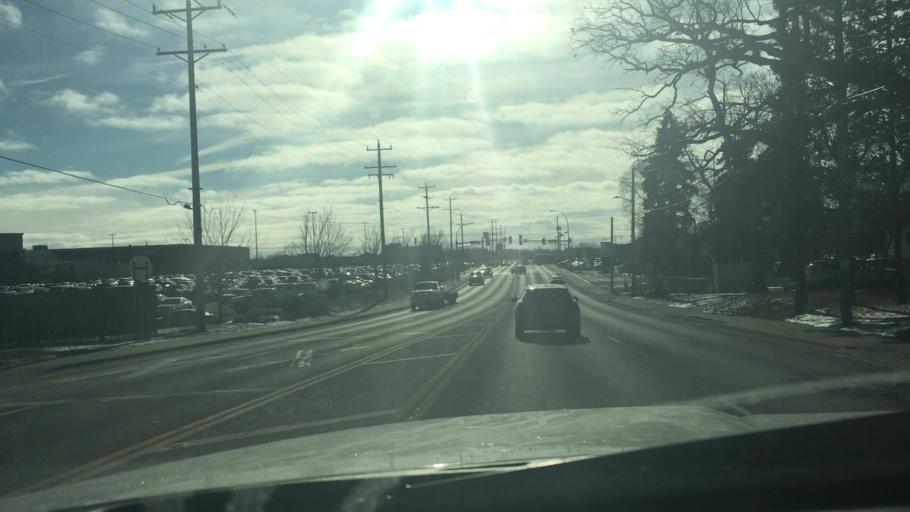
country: US
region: Minnesota
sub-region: Stearns County
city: Waite Park
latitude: 45.5577
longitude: -94.2138
